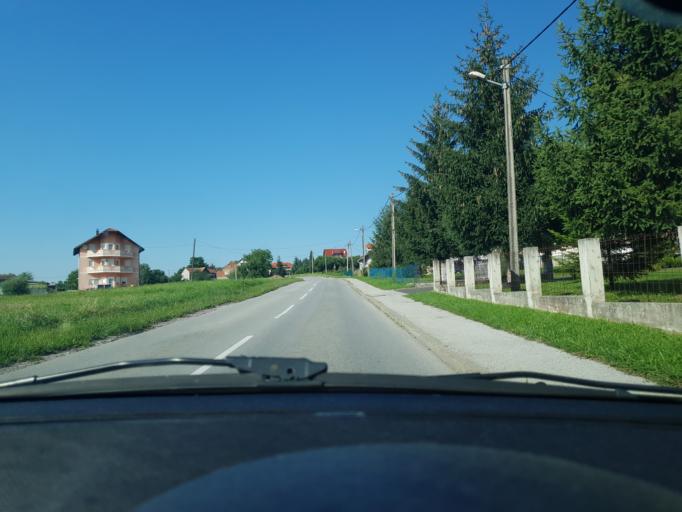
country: HR
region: Zagrebacka
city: Jablanovec
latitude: 45.8752
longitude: 15.8481
